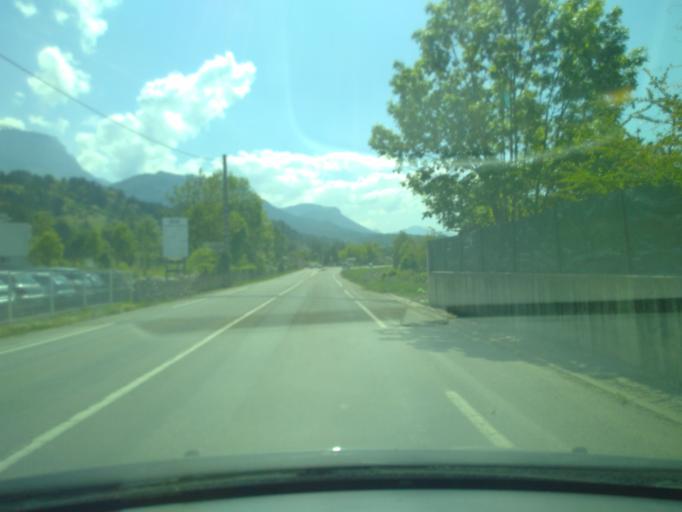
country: FR
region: Rhone-Alpes
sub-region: Departement de la Drome
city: Die
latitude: 44.7472
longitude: 5.3824
